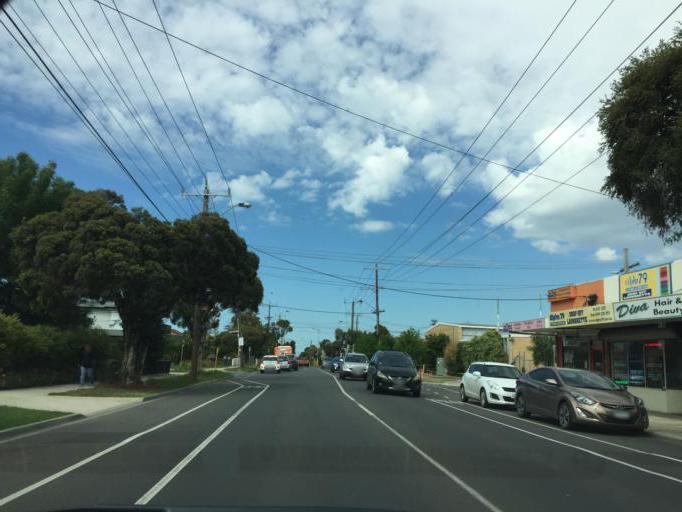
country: AU
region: Victoria
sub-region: Maribyrnong
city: Maribyrnong
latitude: -37.7816
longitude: 144.8844
